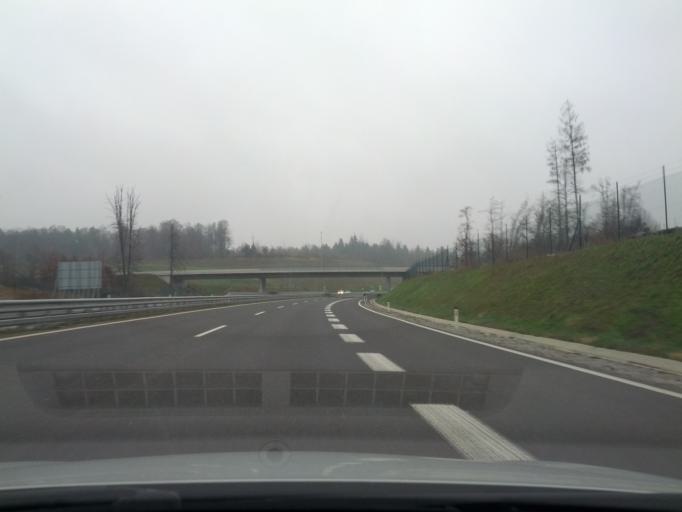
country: SI
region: Trebnje
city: Trebnje
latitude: 45.8994
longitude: 15.0526
